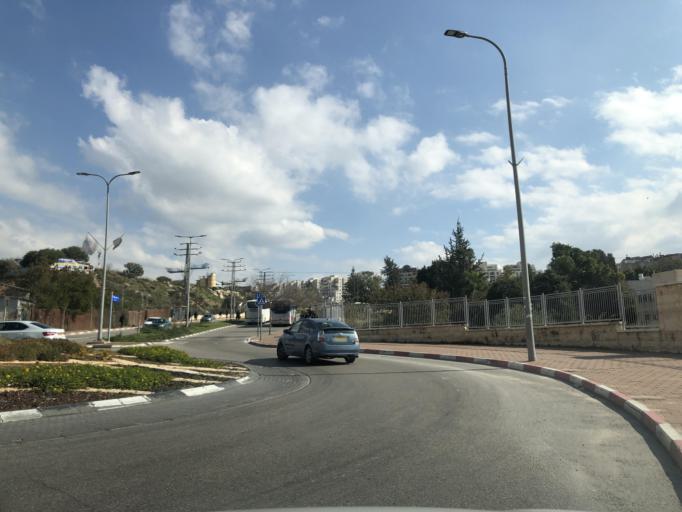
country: IL
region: Jerusalem
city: Modiin Ilit
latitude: 31.9361
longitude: 35.0455
